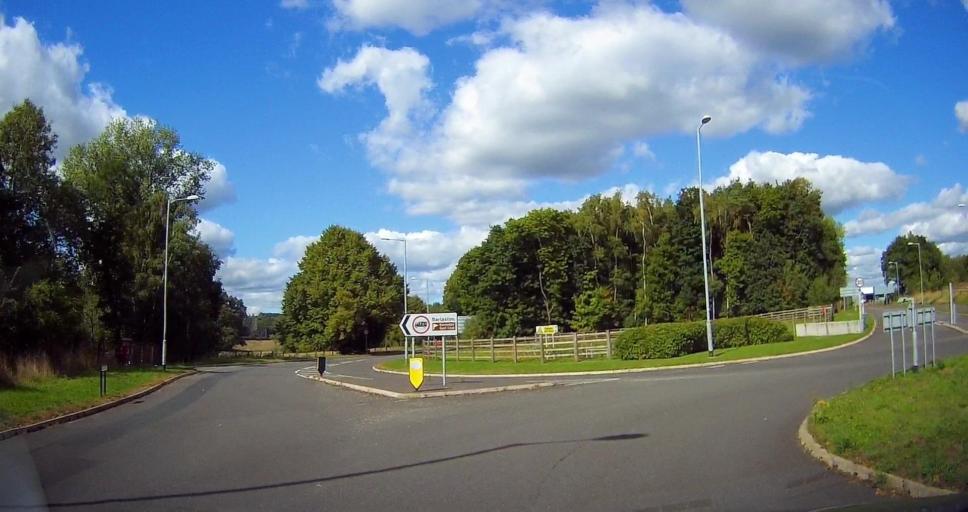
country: GB
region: England
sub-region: Staffordshire
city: Stone
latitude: 52.9183
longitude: -2.1645
